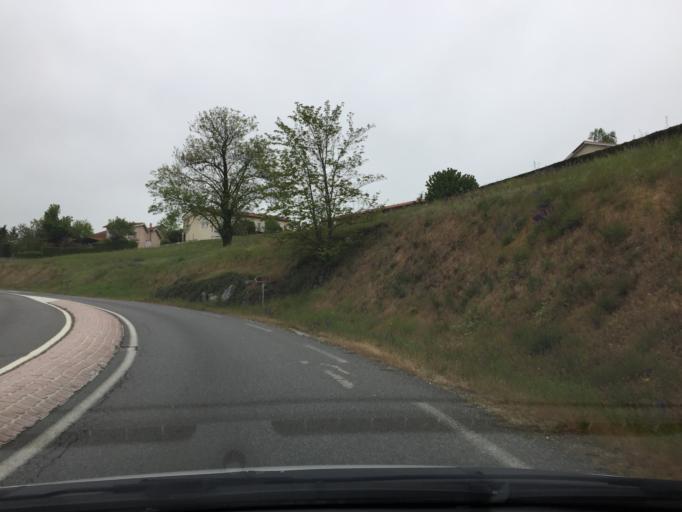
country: FR
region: Rhone-Alpes
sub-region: Departement du Rhone
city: Mornant
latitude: 45.6210
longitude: 4.6669
